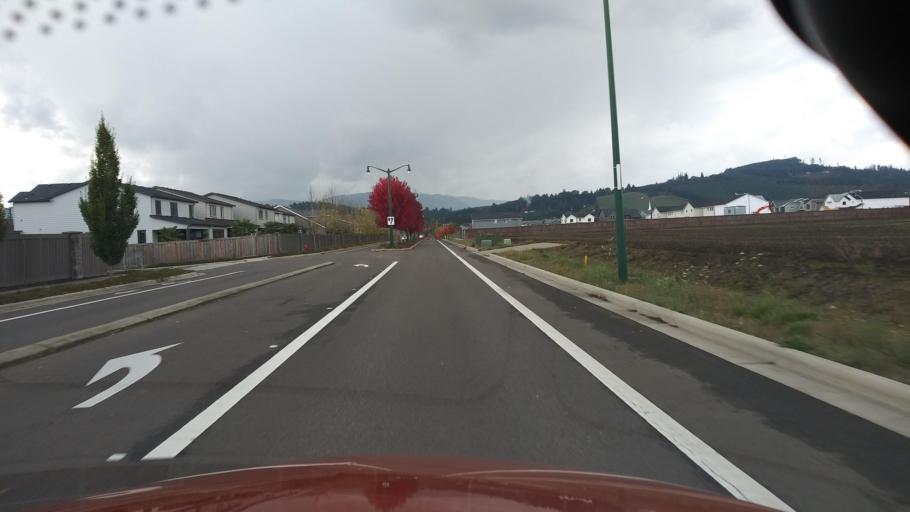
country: US
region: Oregon
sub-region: Washington County
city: Forest Grove
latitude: 45.5391
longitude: -123.1164
